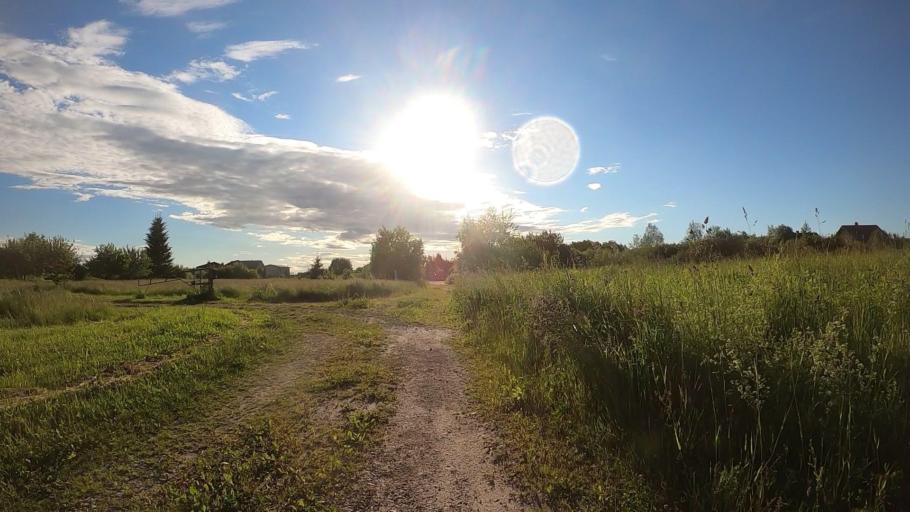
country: LV
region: Salaspils
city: Salaspils
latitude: 56.8421
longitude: 24.3994
